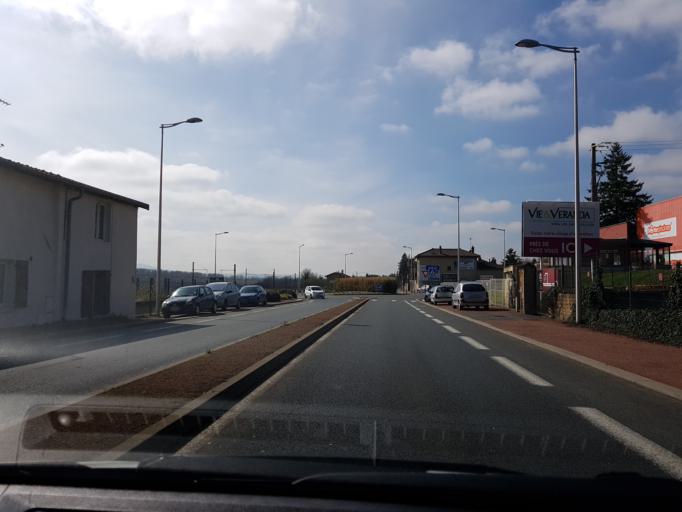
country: FR
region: Rhone-Alpes
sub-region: Departement du Rhone
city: Villefranche-sur-Saone
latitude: 45.9660
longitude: 4.7163
